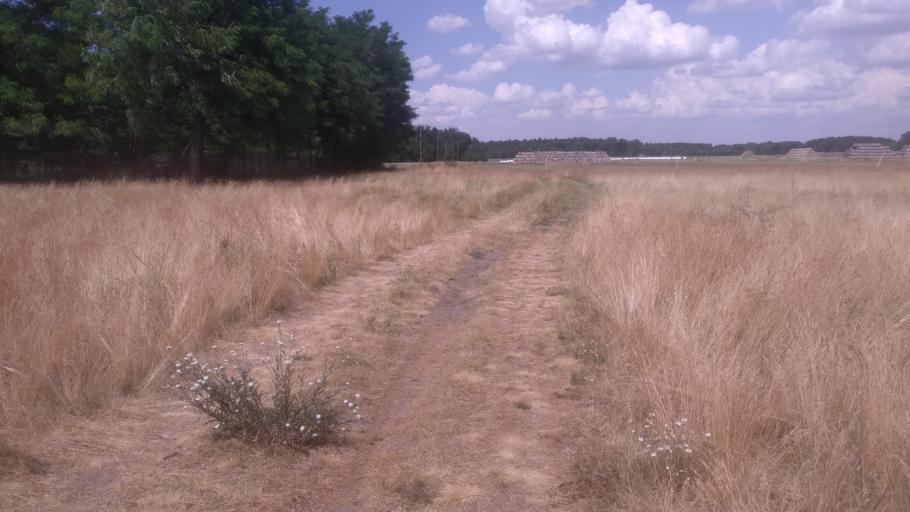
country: HU
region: Pest
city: Cegledbercel
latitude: 47.1870
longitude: 19.7269
